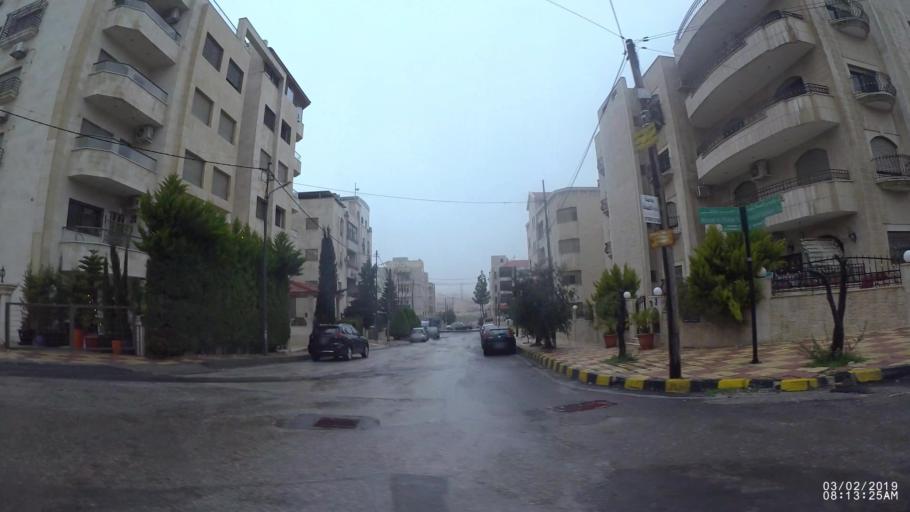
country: JO
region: Amman
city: Wadi as Sir
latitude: 31.9697
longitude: 35.8655
